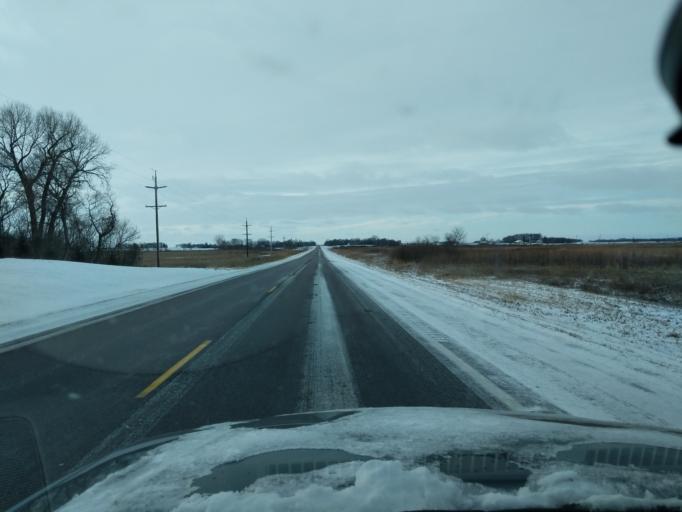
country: US
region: Minnesota
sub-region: McLeod County
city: Hutchinson
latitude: 44.7247
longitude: -94.3910
